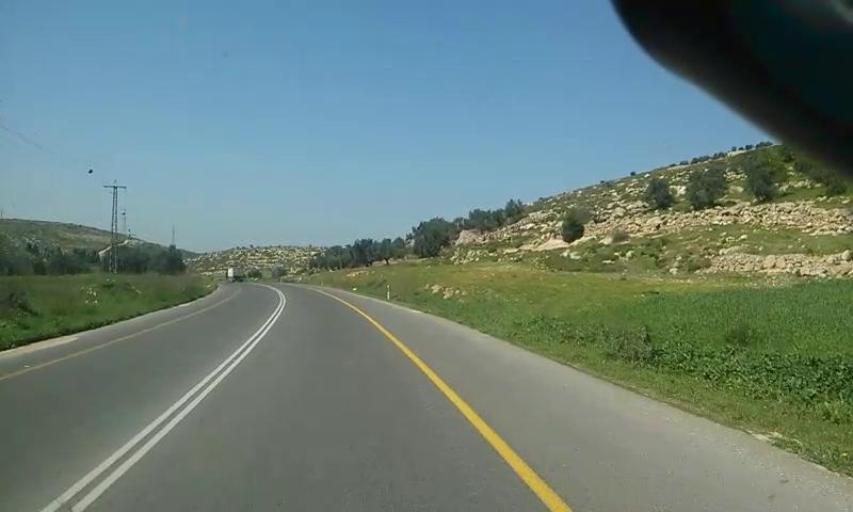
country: PS
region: West Bank
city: Idhna
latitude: 31.5790
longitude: 34.9781
